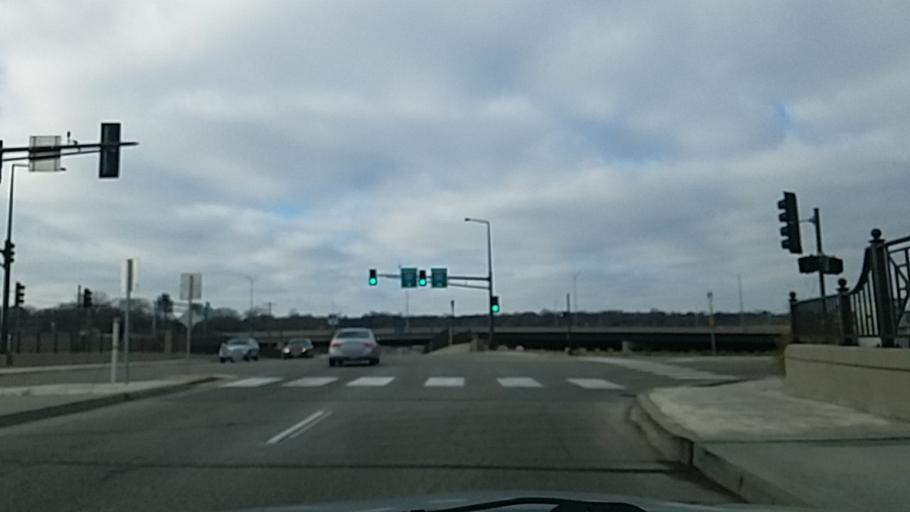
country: US
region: Minnesota
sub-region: Ramsey County
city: Saint Paul
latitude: 44.9666
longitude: -93.0867
